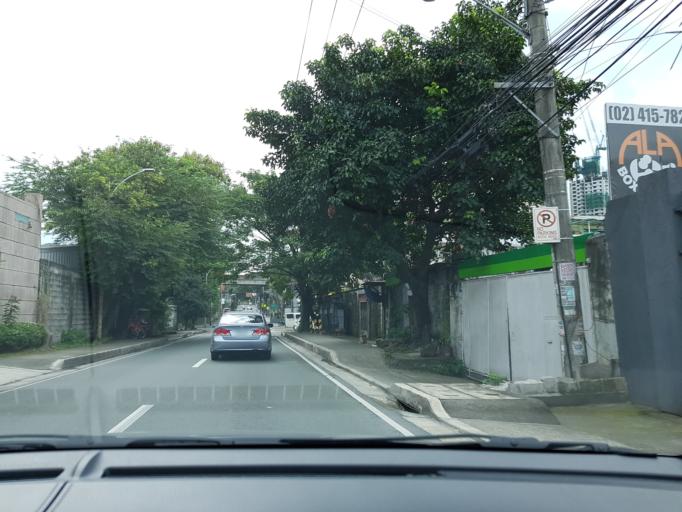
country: PH
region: Metro Manila
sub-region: San Juan
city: San Juan
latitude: 14.6179
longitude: 121.0390
